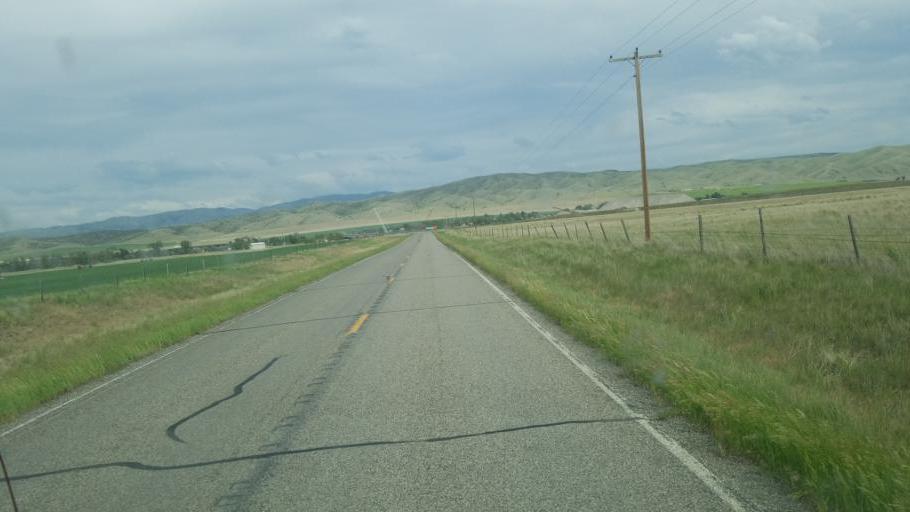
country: US
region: Montana
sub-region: Broadwater County
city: Townsend
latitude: 46.1736
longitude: -111.4604
